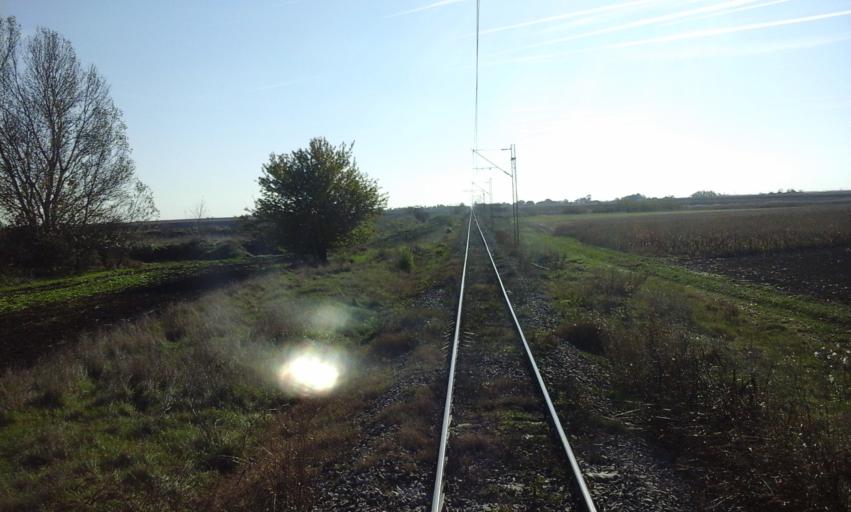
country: RS
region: Autonomna Pokrajina Vojvodina
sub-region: Severnobacki Okrug
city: Subotica
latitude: 46.0006
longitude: 19.6777
